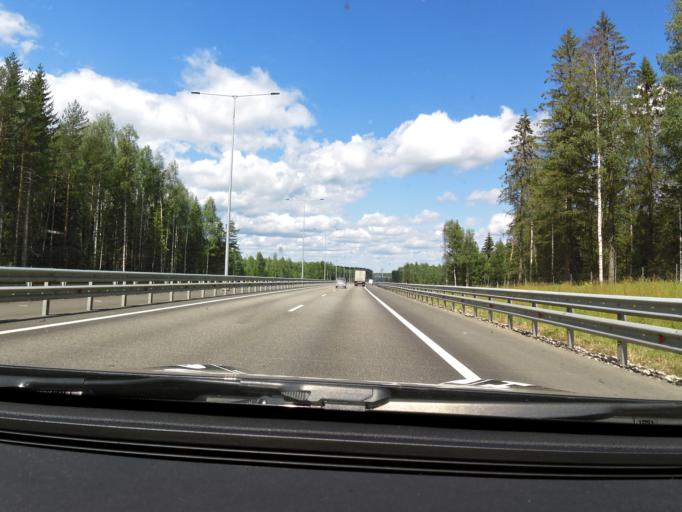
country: RU
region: Tverskaya
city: Vyshniy Volochek
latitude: 57.3878
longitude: 34.5542
